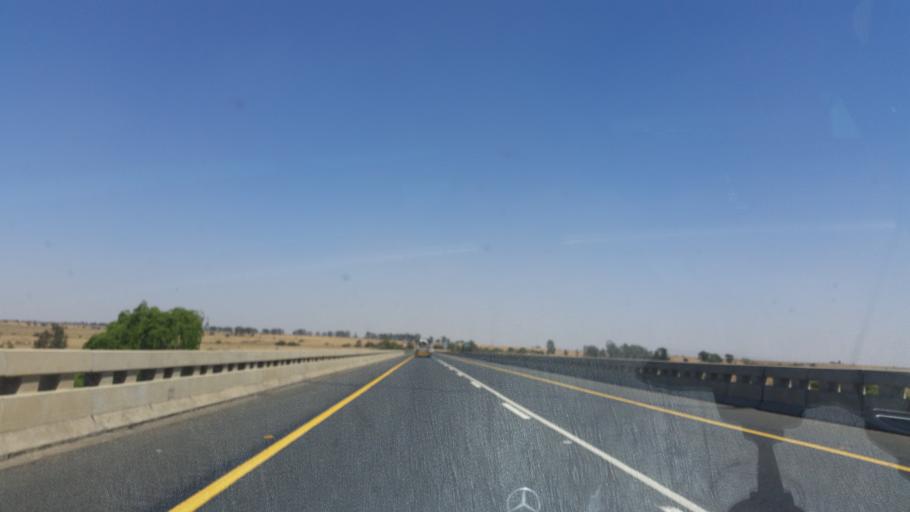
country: ZA
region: Orange Free State
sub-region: Lejweleputswa District Municipality
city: Winburg
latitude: -28.6312
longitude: 26.9043
